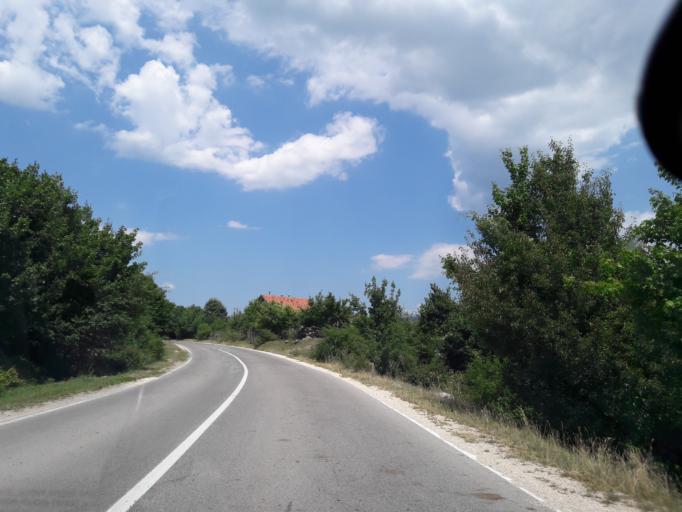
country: BA
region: Republika Srpska
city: Sipovo
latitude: 44.1680
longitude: 17.1677
